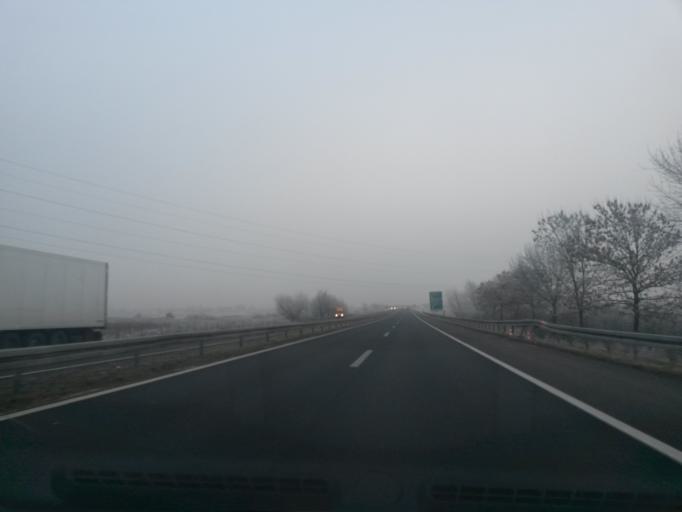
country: HR
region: Zagrebacka
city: Brckovljani
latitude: 45.8938
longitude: 16.2531
